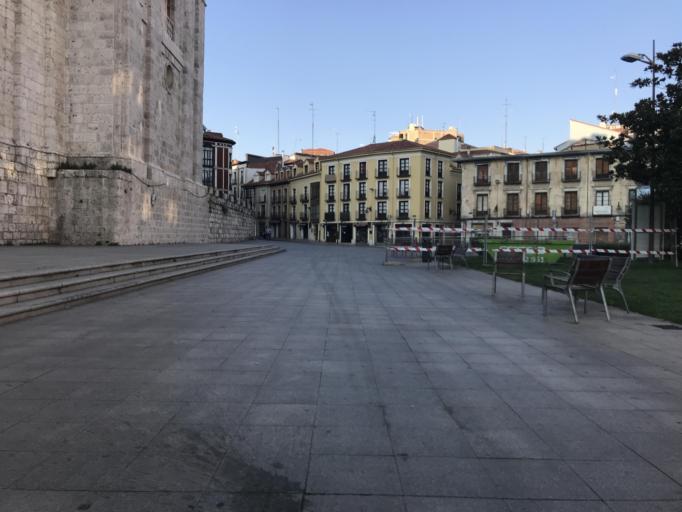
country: ES
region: Castille and Leon
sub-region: Provincia de Valladolid
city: Valladolid
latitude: 41.6531
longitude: -4.7236
